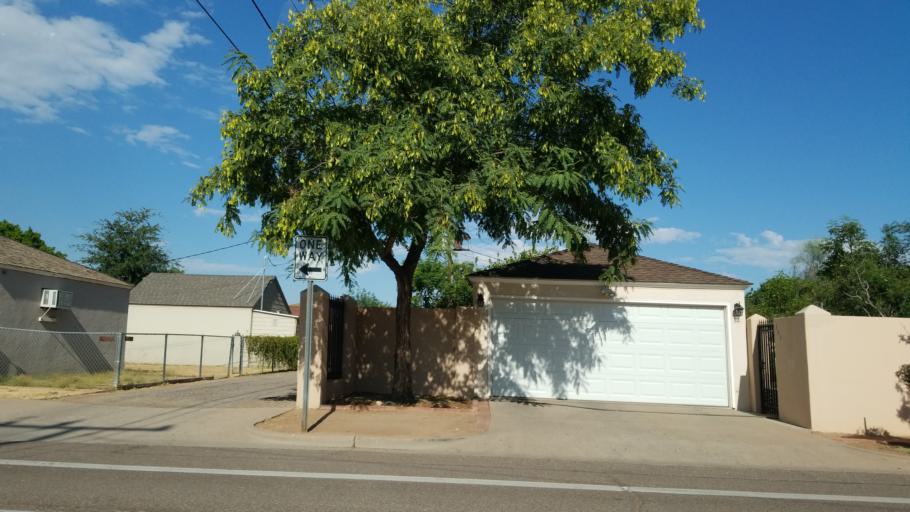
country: US
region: Arizona
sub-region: Maricopa County
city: Phoenix
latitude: 33.4772
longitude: -112.0804
